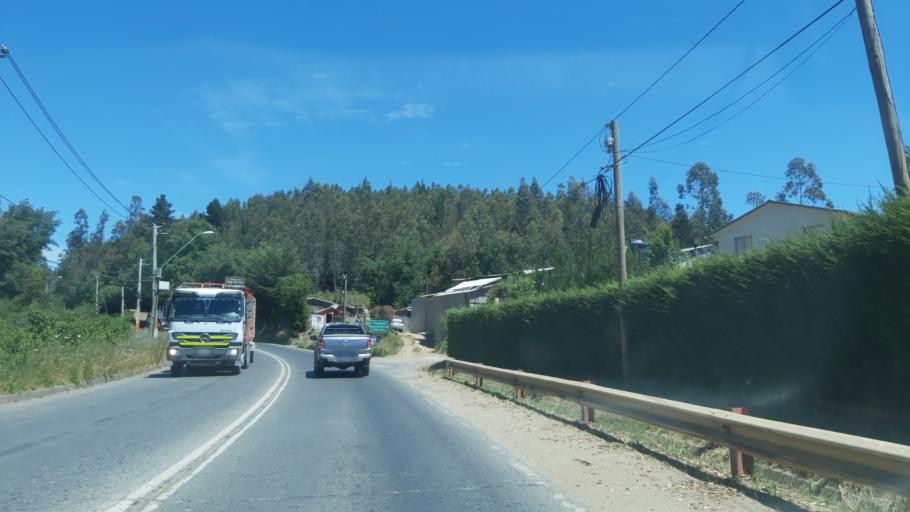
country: CL
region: Maule
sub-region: Provincia de Talca
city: Constitucion
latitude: -35.3536
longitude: -72.4105
